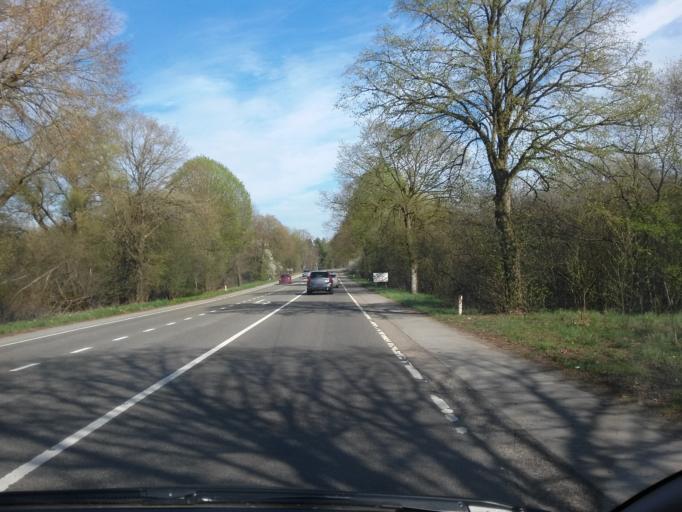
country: BE
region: Wallonia
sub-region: Province du Luxembourg
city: Arlon
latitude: 49.6920
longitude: 5.7786
